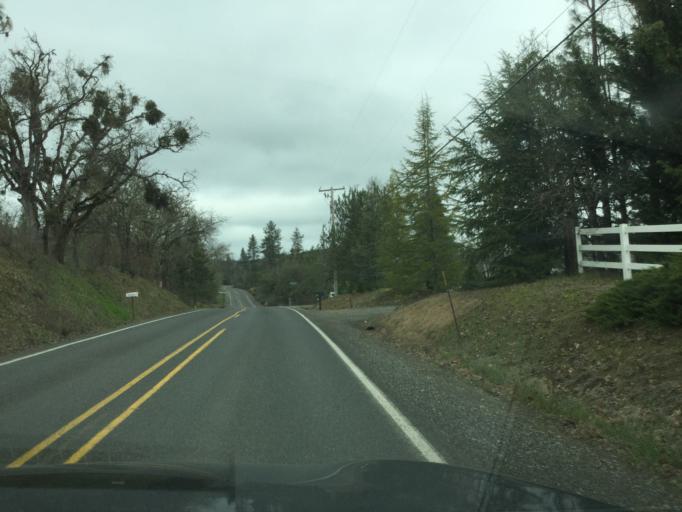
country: US
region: Oregon
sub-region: Jackson County
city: Central Point
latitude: 42.3839
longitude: -122.9702
